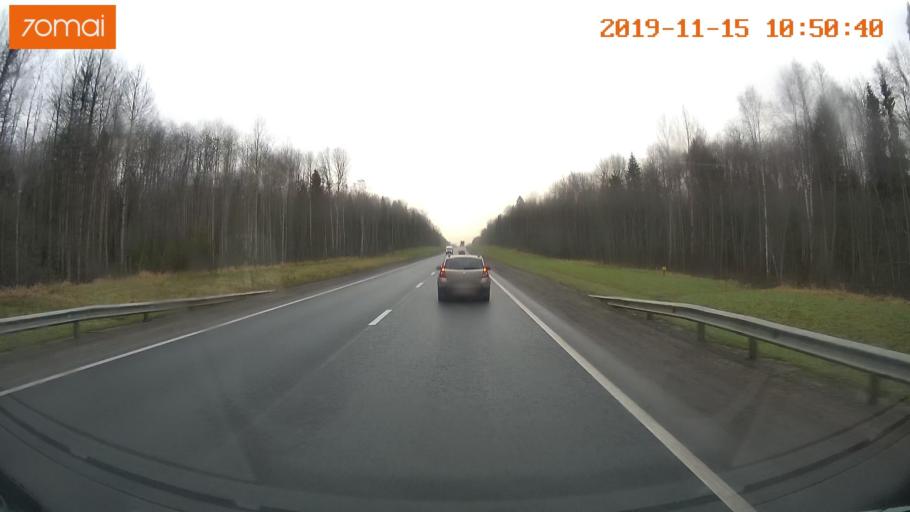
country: RU
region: Vologda
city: Chebsara
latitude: 59.1841
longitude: 38.6869
